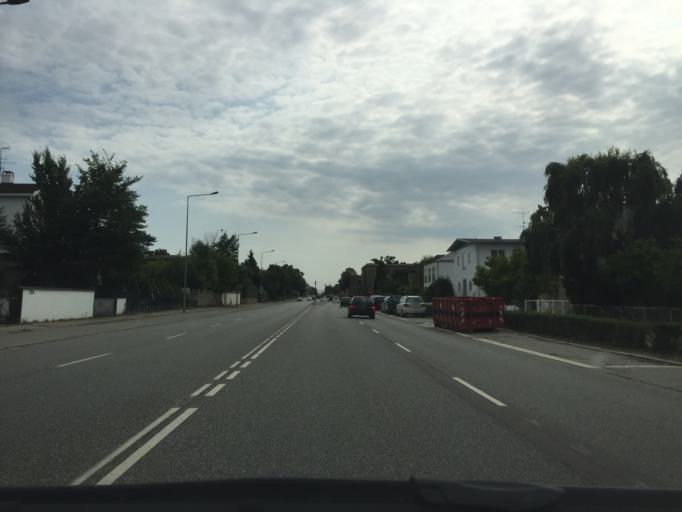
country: DK
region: Capital Region
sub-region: Gentofte Kommune
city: Charlottenlund
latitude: 55.7517
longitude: 12.5577
